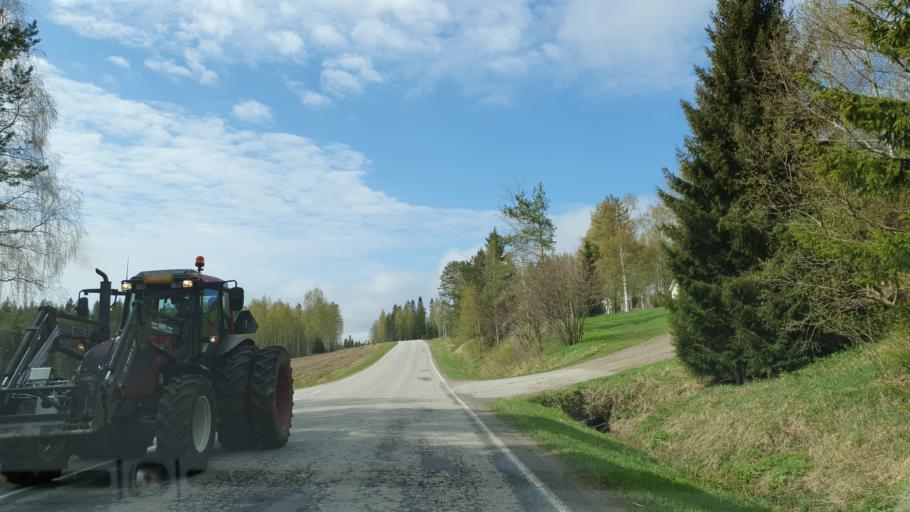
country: FI
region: Kainuu
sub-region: Kehys-Kainuu
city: Kuhmo
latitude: 64.1248
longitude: 29.6489
